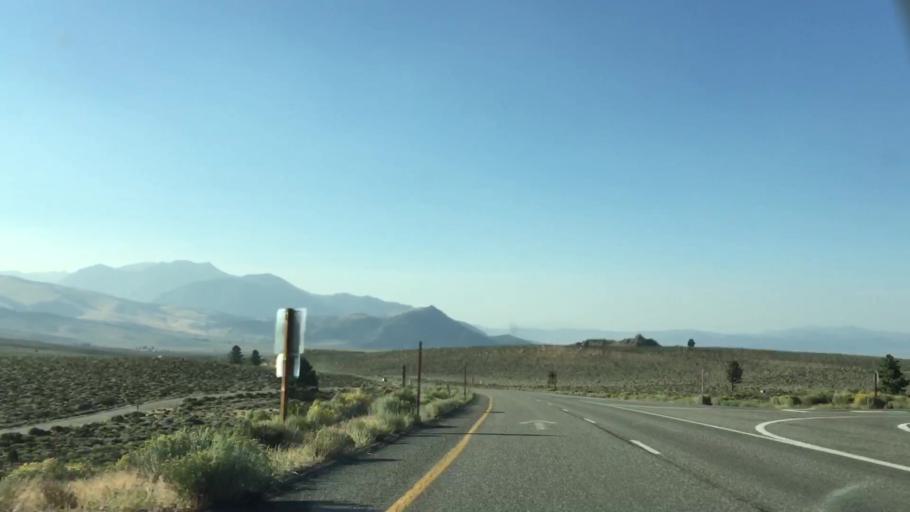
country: US
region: California
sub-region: Mono County
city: Mammoth Lakes
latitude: 37.8398
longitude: -119.0707
